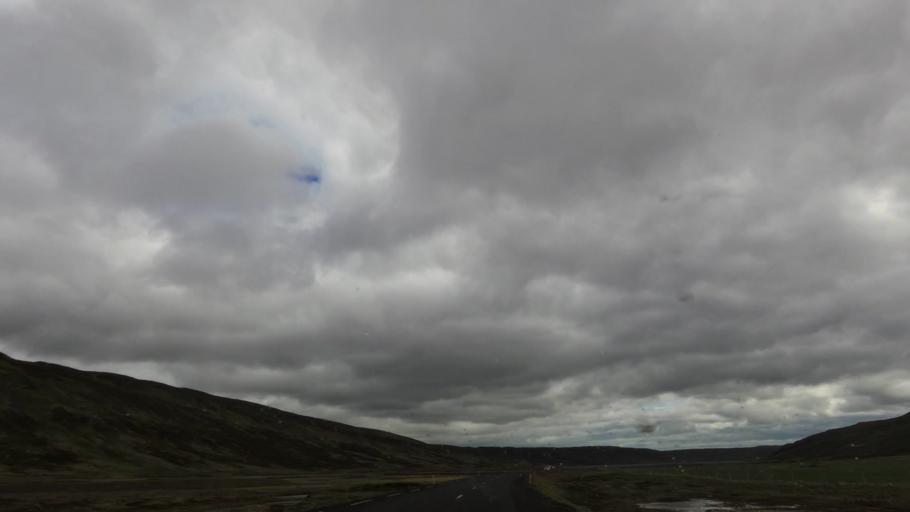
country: IS
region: West
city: Stykkisholmur
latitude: 65.7668
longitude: -21.8269
